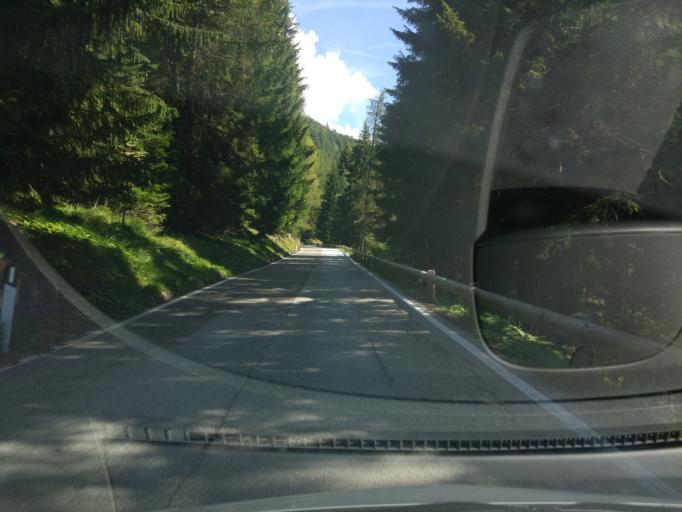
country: IT
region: Trentino-Alto Adige
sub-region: Provincia di Trento
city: Moena
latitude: 46.3084
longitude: 11.6888
